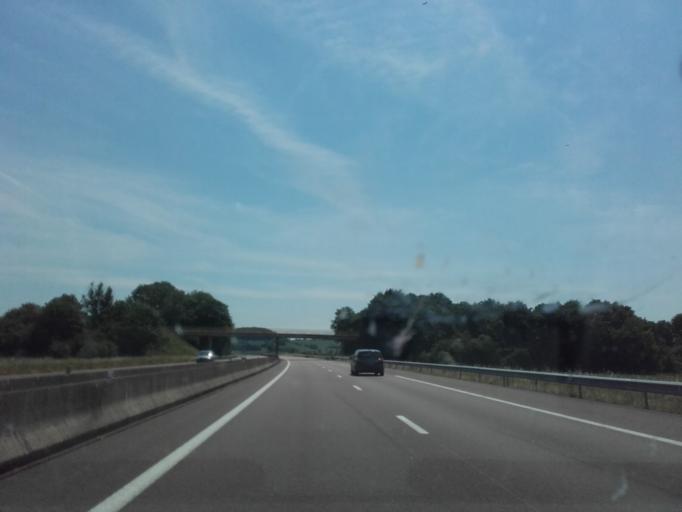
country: FR
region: Bourgogne
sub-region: Departement de la Cote-d'Or
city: Pouilly-en-Auxois
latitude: 47.2598
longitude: 4.5251
